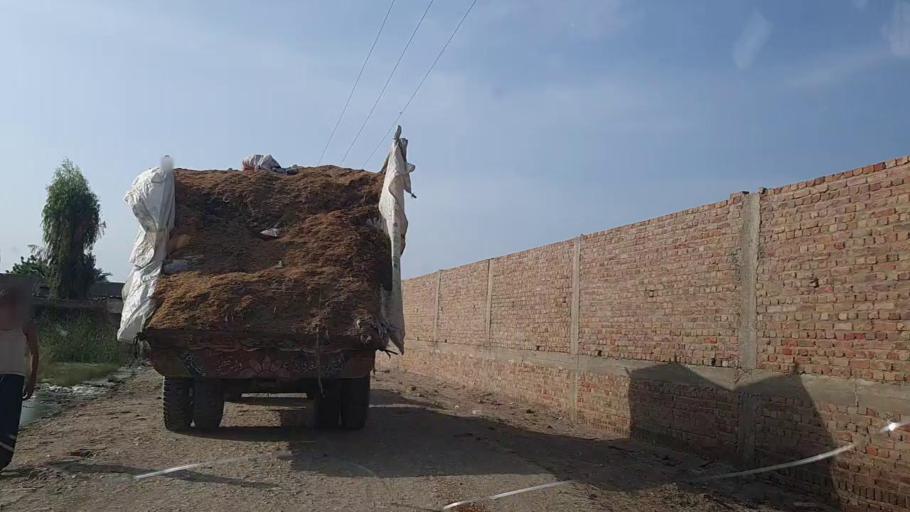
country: PK
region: Sindh
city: Ghotki
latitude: 28.0110
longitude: 69.2951
